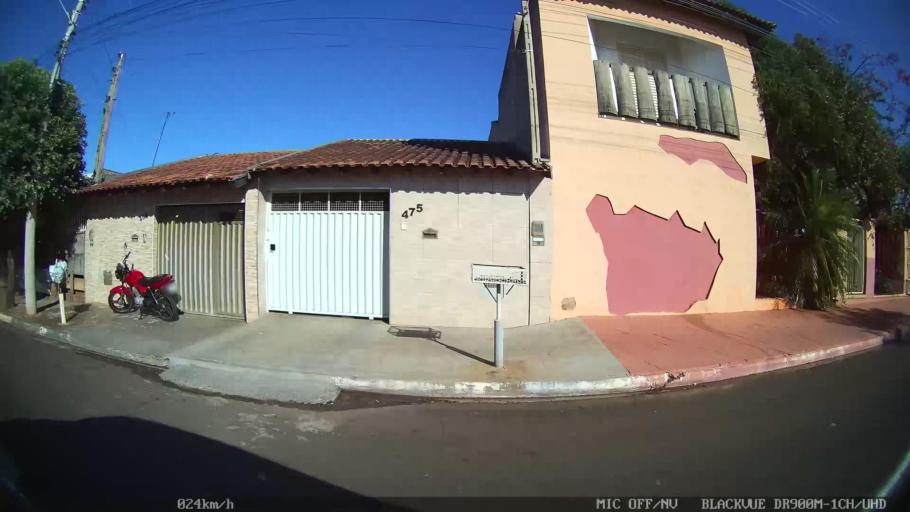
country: BR
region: Sao Paulo
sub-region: Olimpia
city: Olimpia
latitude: -20.7250
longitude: -48.8940
